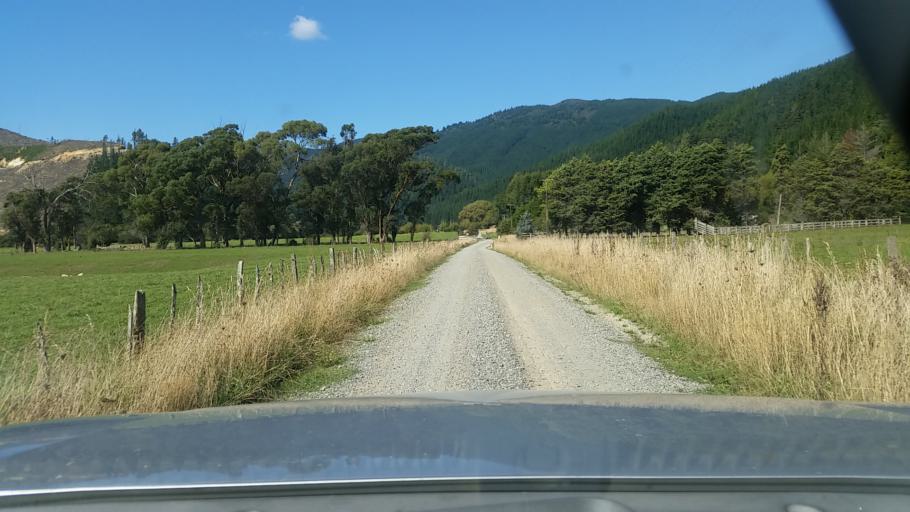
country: NZ
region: Marlborough
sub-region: Marlborough District
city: Blenheim
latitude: -41.4072
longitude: 173.7876
